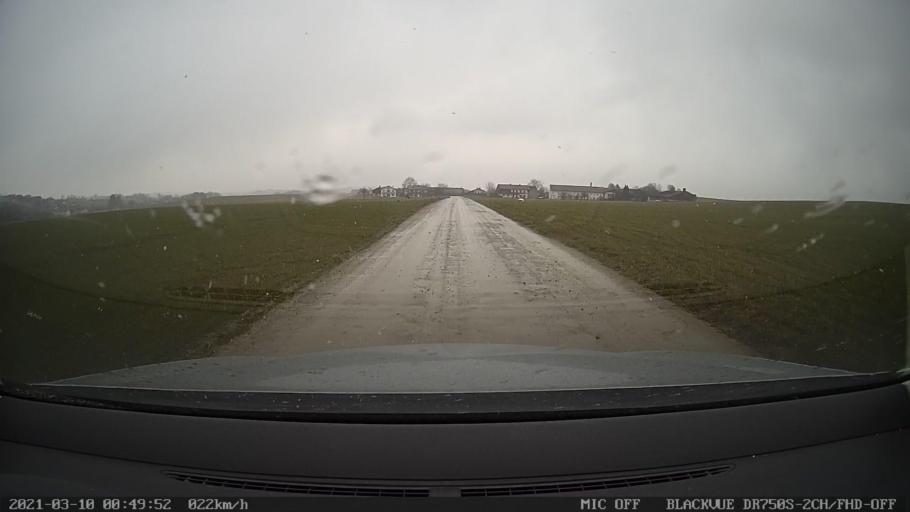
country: DE
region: Bavaria
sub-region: Upper Bavaria
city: Griesstatt
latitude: 47.9935
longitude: 12.1883
